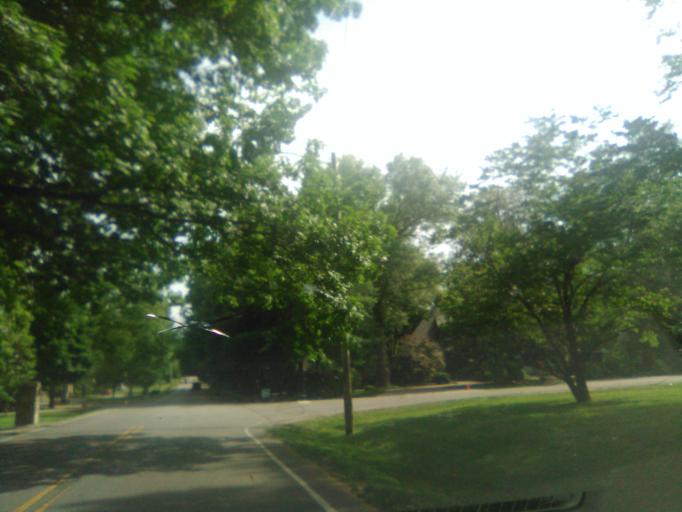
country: US
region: Tennessee
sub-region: Davidson County
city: Belle Meade
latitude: 36.0945
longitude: -86.8693
